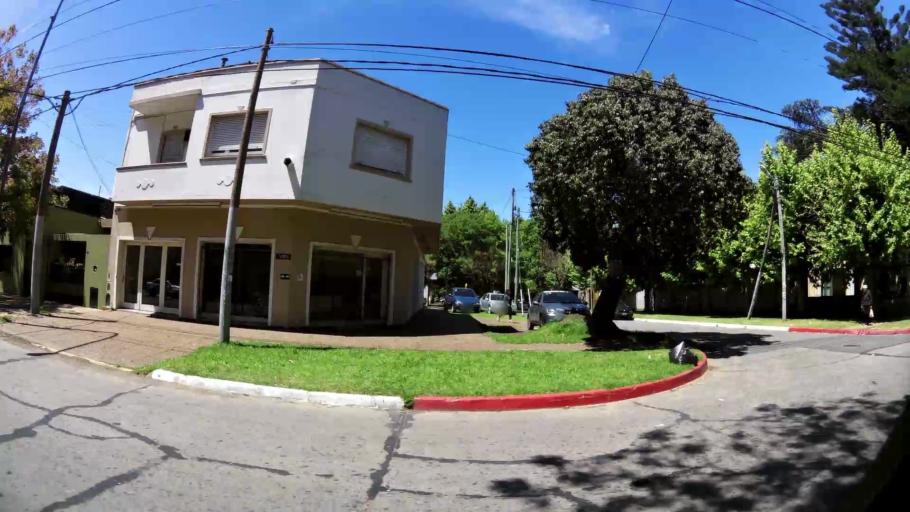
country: AR
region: Buenos Aires
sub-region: Partido de Quilmes
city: Quilmes
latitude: -34.7139
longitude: -58.2791
